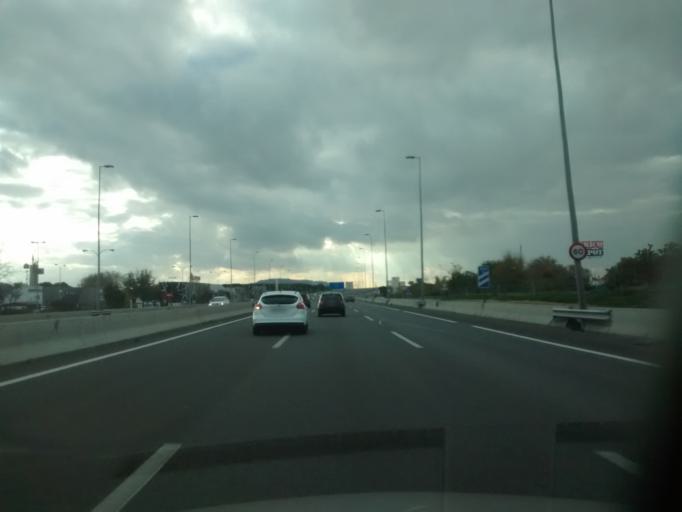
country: ES
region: Madrid
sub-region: Provincia de Madrid
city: Alcala de Henares
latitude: 40.5053
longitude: -3.3302
